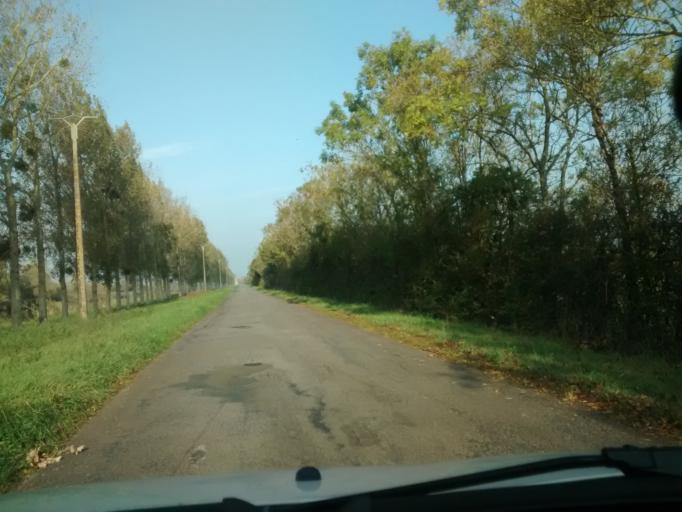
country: FR
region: Pays de la Loire
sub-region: Departement de la Loire-Atlantique
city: Vue
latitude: 47.2293
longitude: -1.8523
